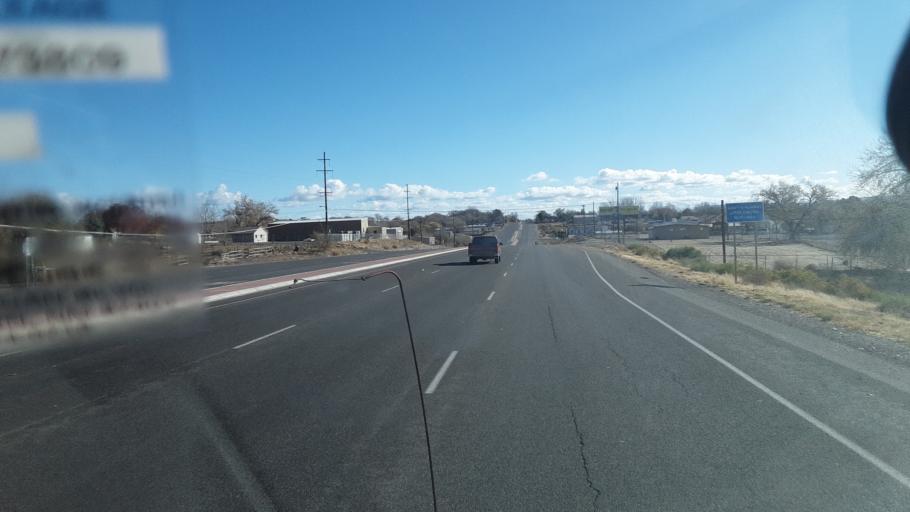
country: US
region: New Mexico
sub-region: San Juan County
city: Lee Acres
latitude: 36.7010
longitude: -108.0689
